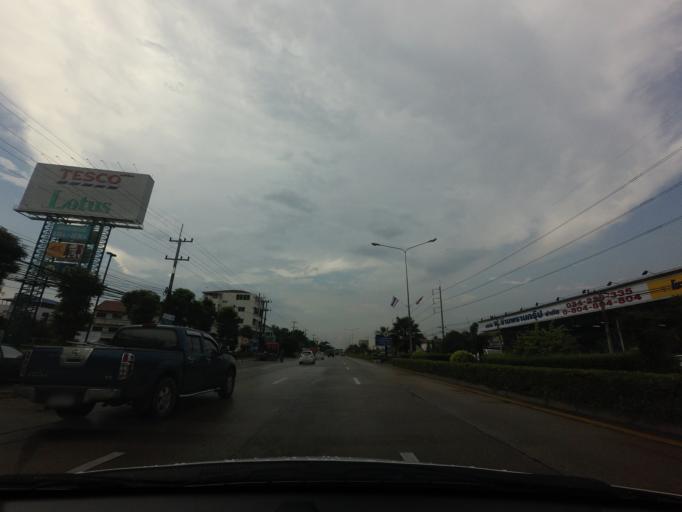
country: TH
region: Nakhon Pathom
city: Sam Phran
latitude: 13.7449
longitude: 100.2196
